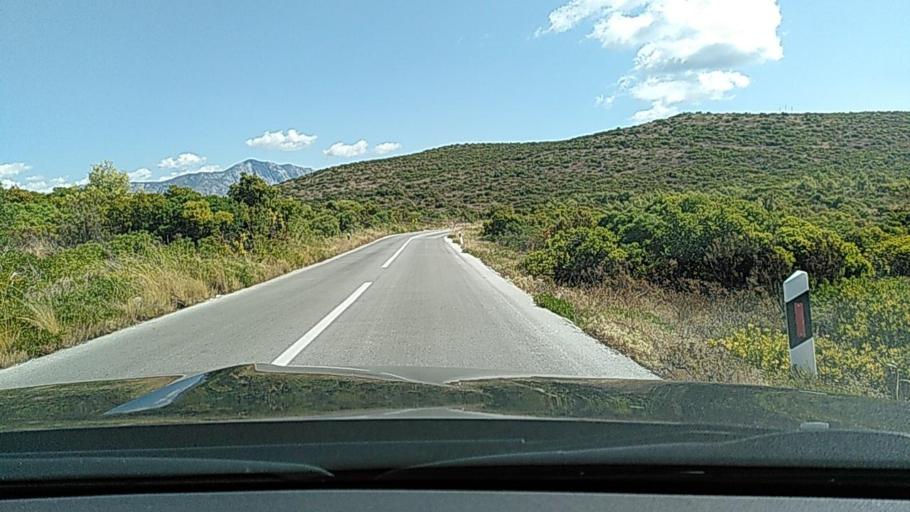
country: HR
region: Splitsko-Dalmatinska
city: Tucepi
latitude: 43.1255
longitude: 17.1029
